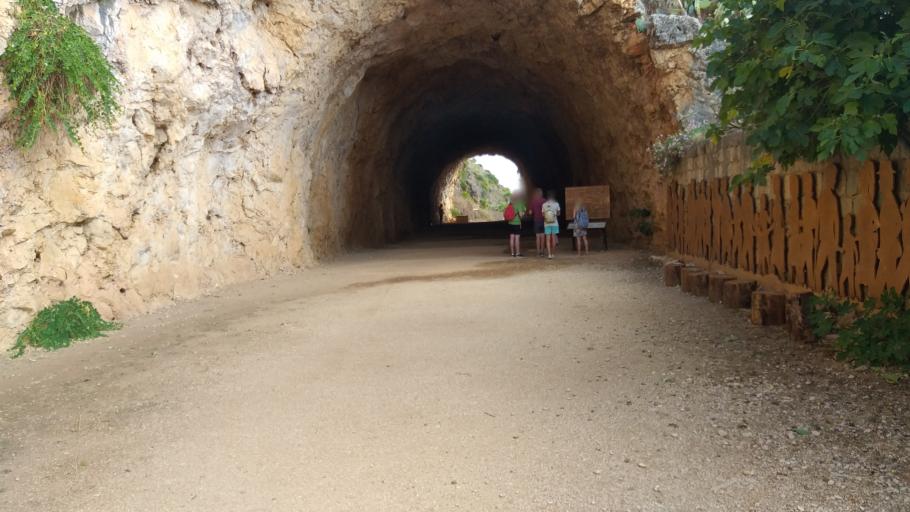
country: IT
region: Sicily
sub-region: Trapani
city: Castelluzzo
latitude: 38.0827
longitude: 12.8074
